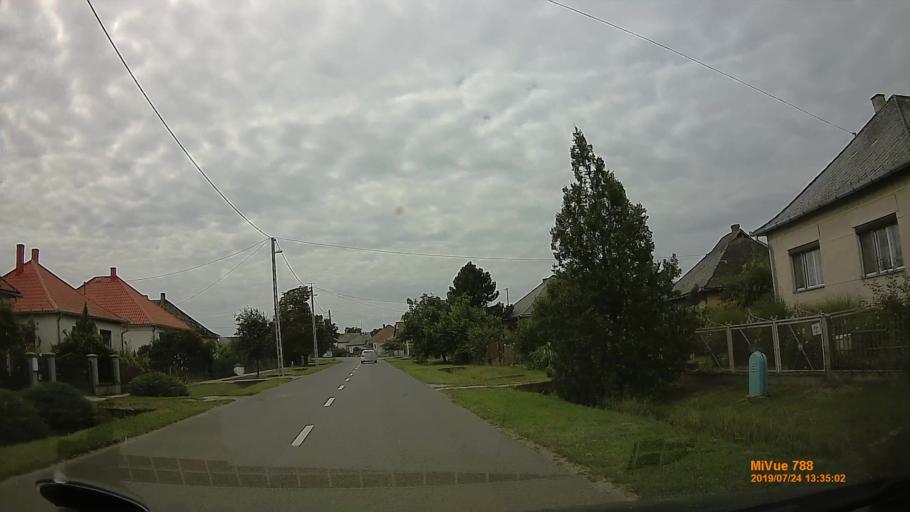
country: HU
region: Szabolcs-Szatmar-Bereg
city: Aranyosapati
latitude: 48.2275
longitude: 22.2968
